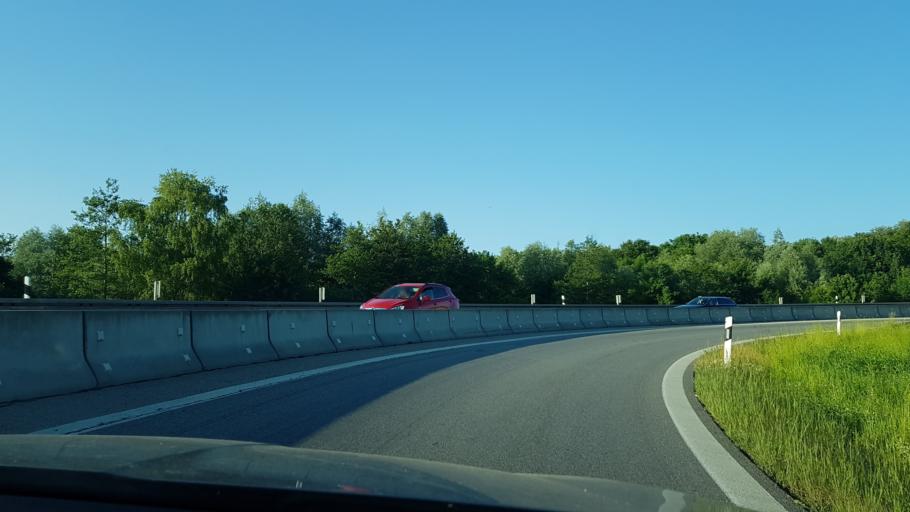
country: DE
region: Bavaria
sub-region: Upper Bavaria
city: Eching
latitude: 48.3223
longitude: 11.6304
